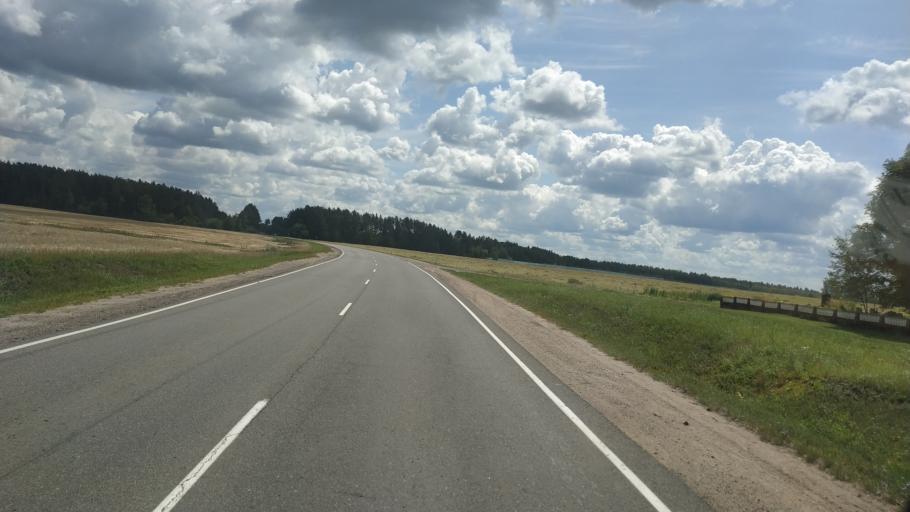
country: BY
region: Mogilev
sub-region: Mahilyowski Rayon
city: Veyno
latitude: 53.8328
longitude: 30.4031
